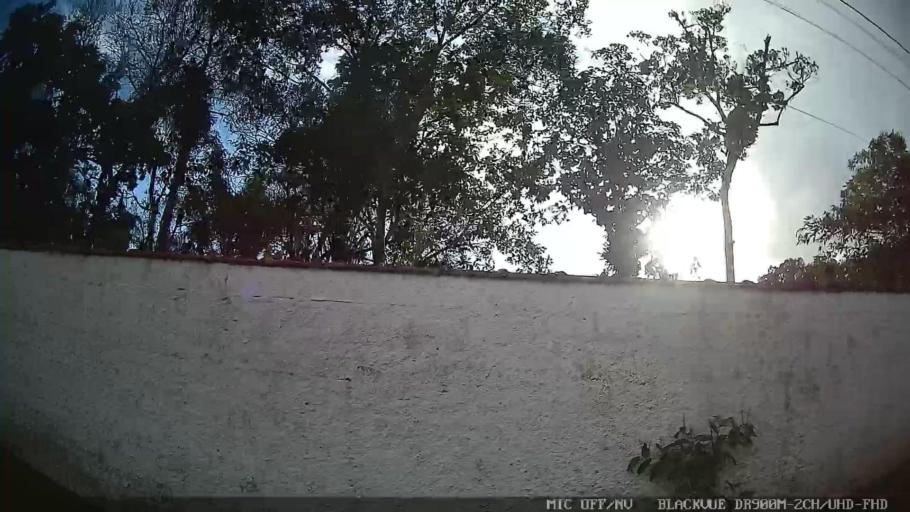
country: BR
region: Sao Paulo
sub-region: Peruibe
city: Peruibe
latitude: -24.2263
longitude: -46.9137
